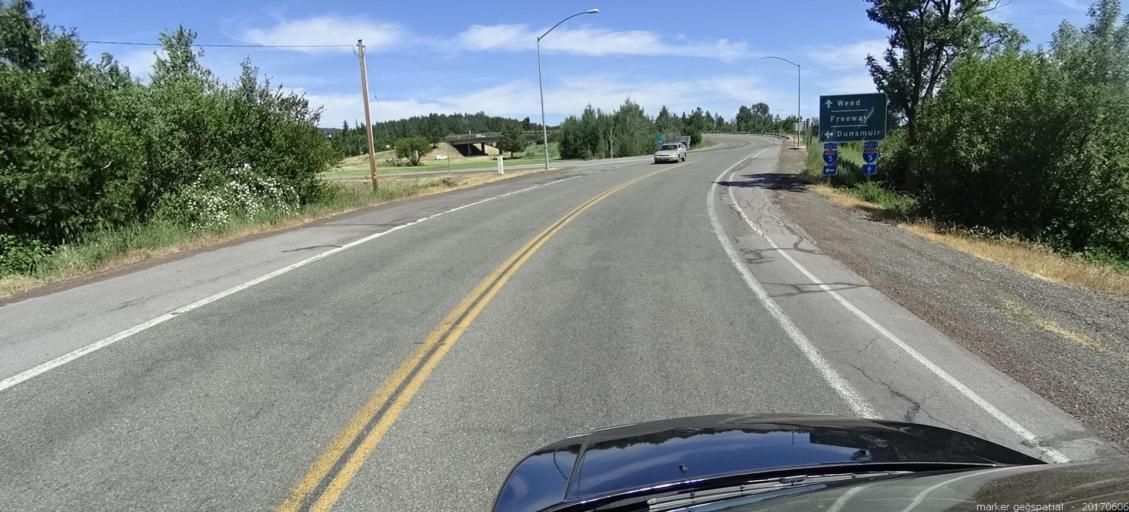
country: US
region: California
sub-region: Siskiyou County
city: Mount Shasta
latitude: 41.3109
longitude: -122.3228
